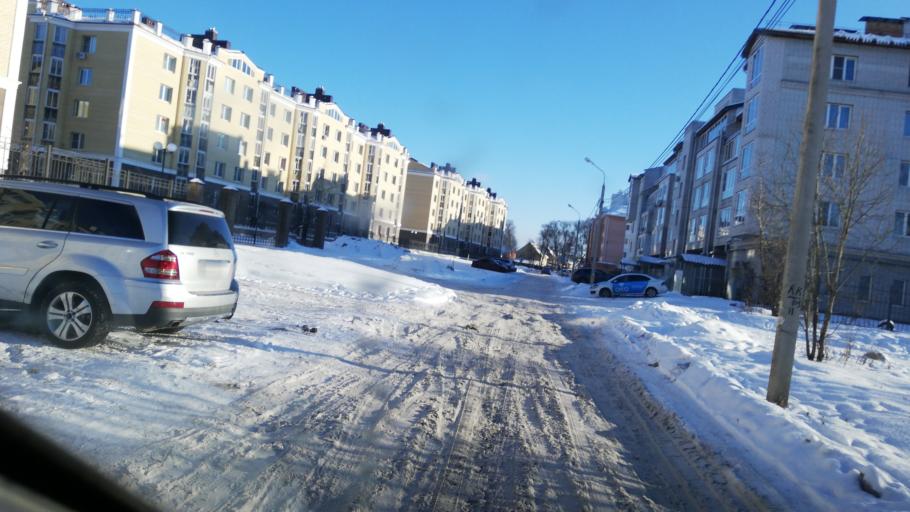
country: RU
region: Jaroslavl
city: Yaroslavl
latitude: 57.6111
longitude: 39.8972
